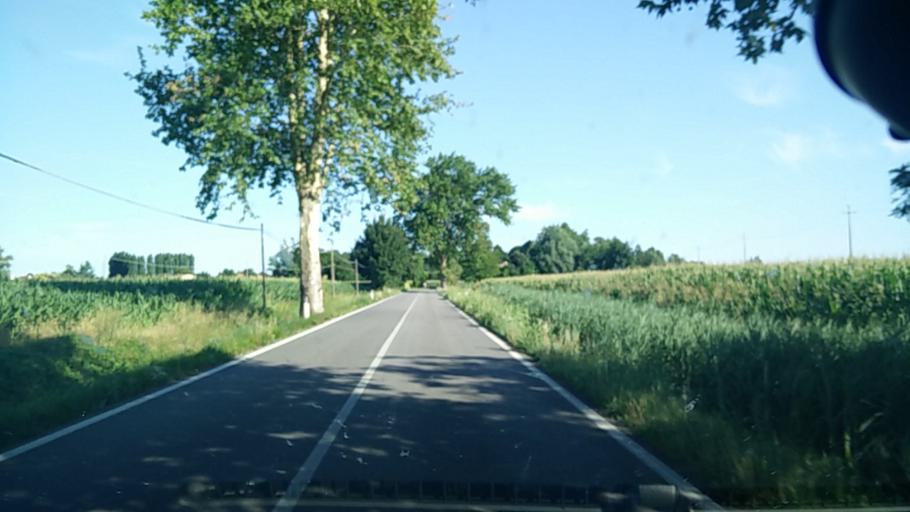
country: IT
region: Veneto
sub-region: Provincia di Treviso
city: Monastier di Treviso
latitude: 45.6626
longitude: 12.4156
